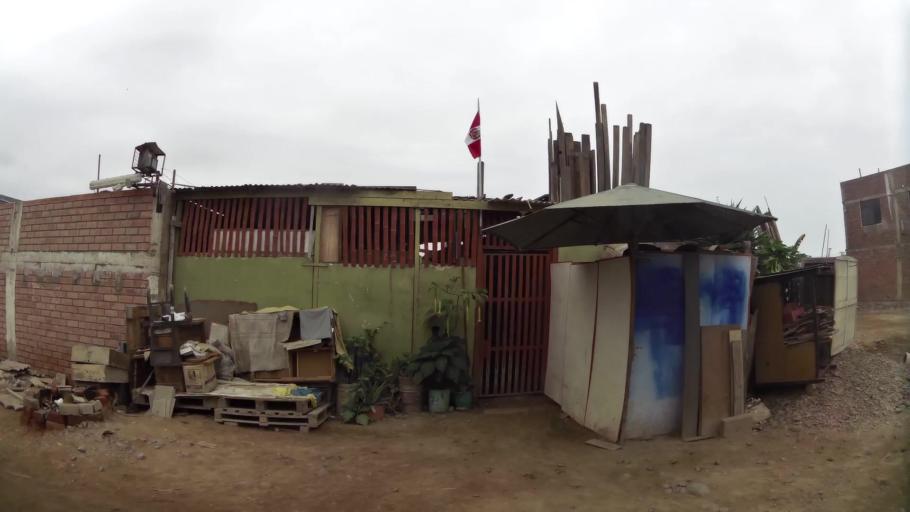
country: PE
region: Lima
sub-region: Lima
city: Surco
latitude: -12.2054
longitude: -77.0037
